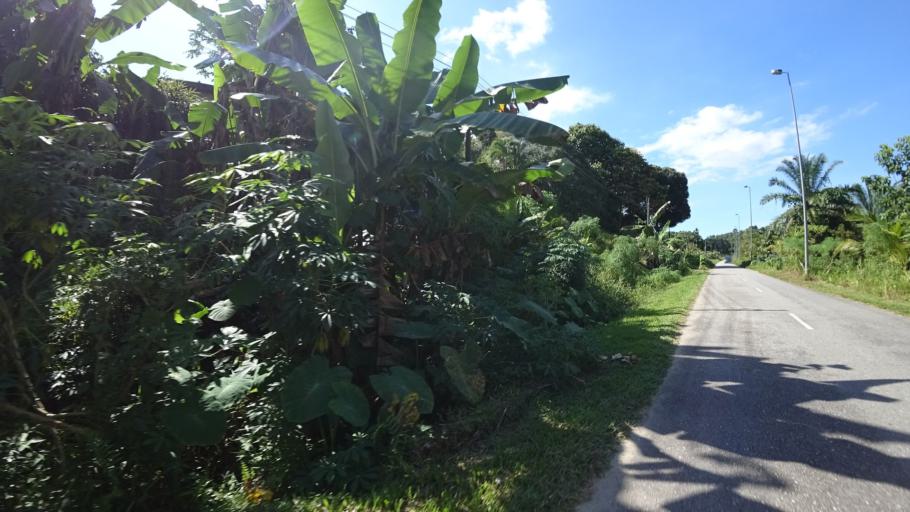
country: BN
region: Tutong
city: Tutong
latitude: 4.7395
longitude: 114.7902
